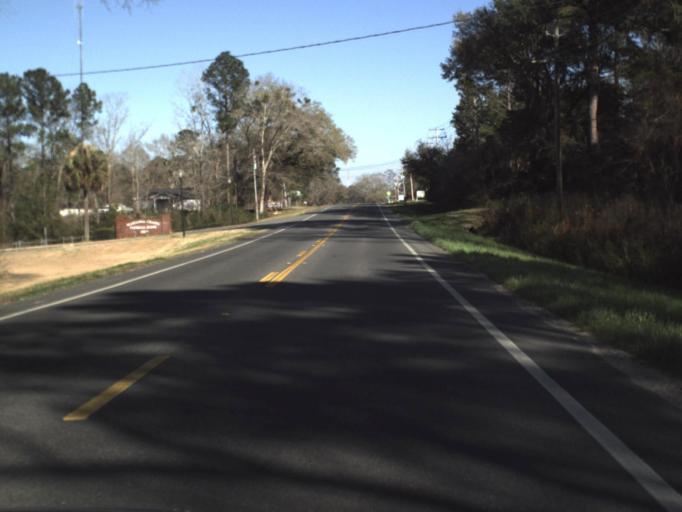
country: US
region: Florida
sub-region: Jackson County
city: Marianna
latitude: 30.7840
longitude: -85.2671
